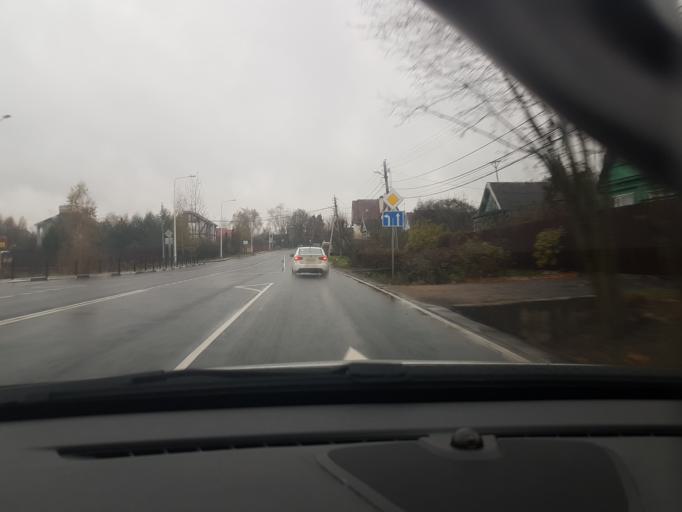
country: RU
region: Moskovskaya
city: Rozhdestveno
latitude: 55.8424
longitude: 37.0017
